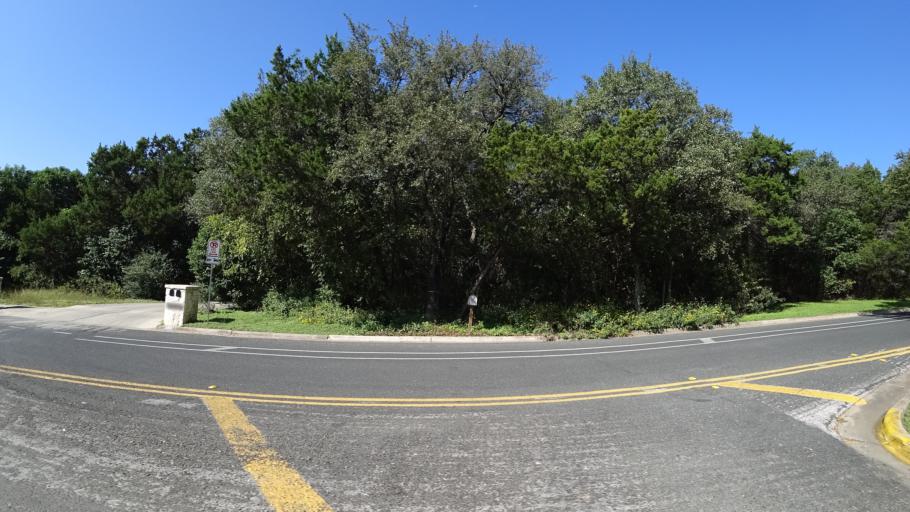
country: US
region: Texas
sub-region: Travis County
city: Rollingwood
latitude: 30.2718
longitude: -97.8111
